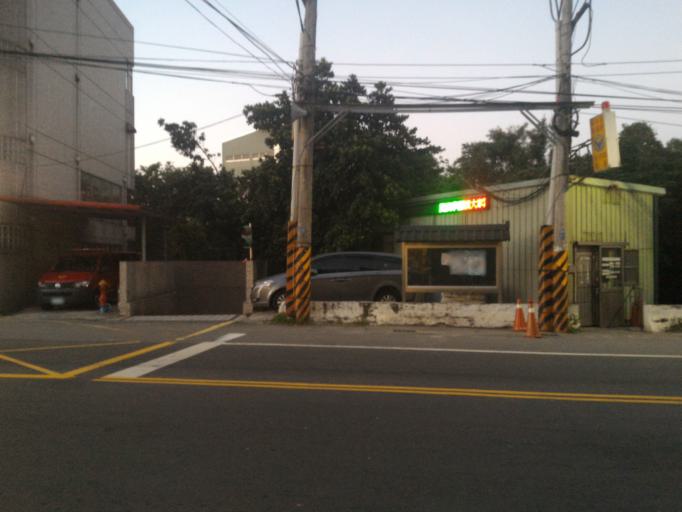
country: TW
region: Taipei
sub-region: Taipei
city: Banqiao
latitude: 24.9602
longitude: 121.4032
